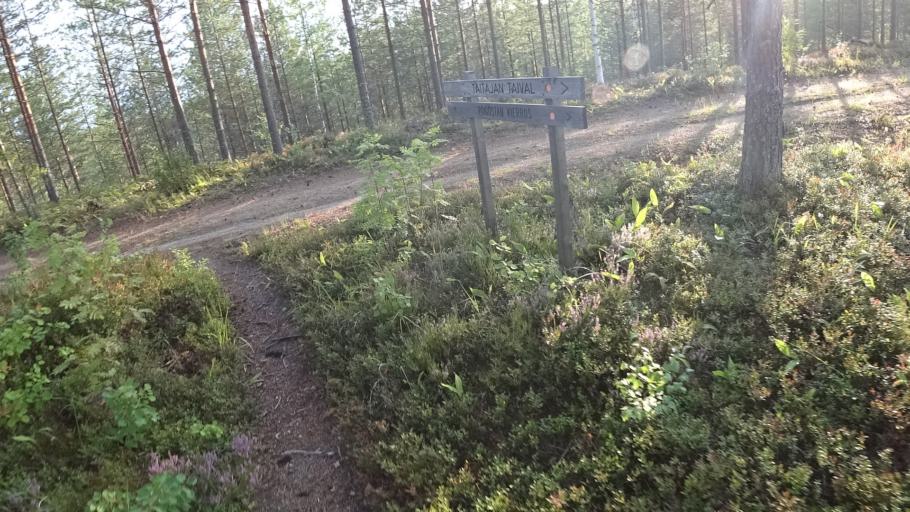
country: FI
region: North Karelia
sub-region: Joensuu
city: Ilomantsi
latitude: 62.6350
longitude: 31.0763
